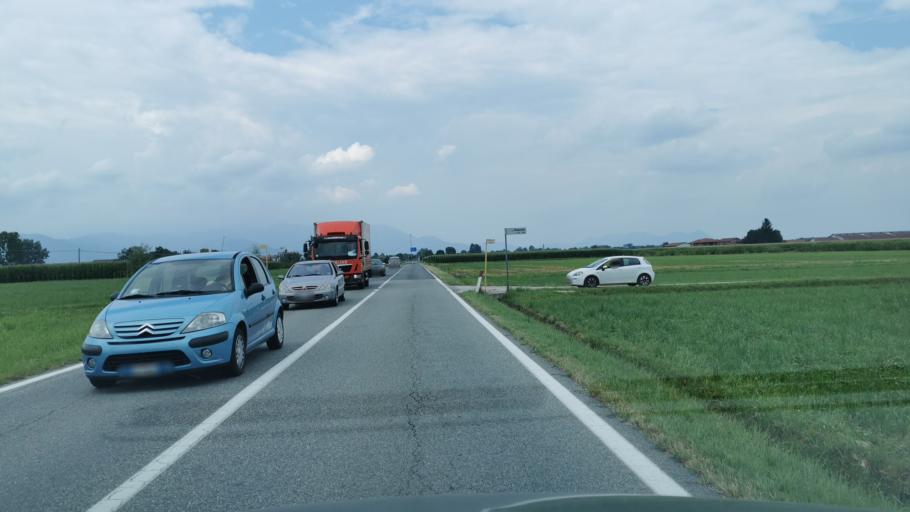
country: IT
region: Piedmont
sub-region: Provincia di Torino
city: Cavour
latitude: 44.8117
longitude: 7.3720
